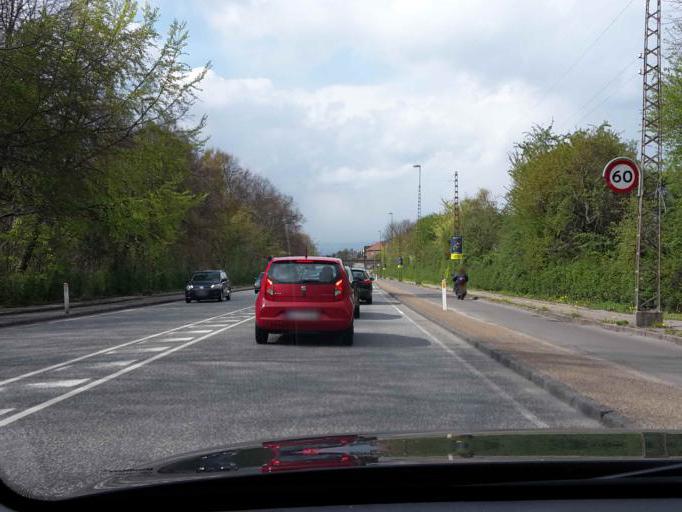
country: DK
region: South Denmark
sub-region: Odense Kommune
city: Odense
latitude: 55.3868
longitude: 10.3538
